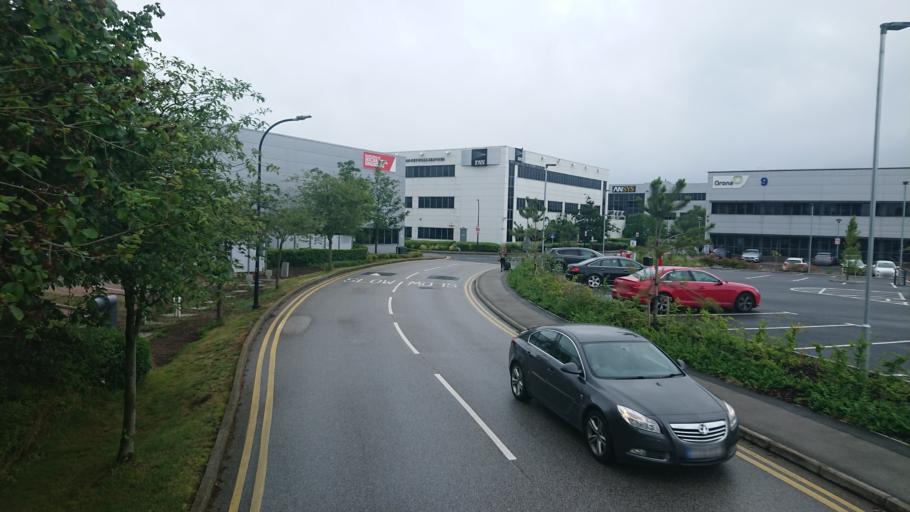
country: GB
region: England
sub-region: Rotherham
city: Orgreave
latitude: 53.3959
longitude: -1.3858
